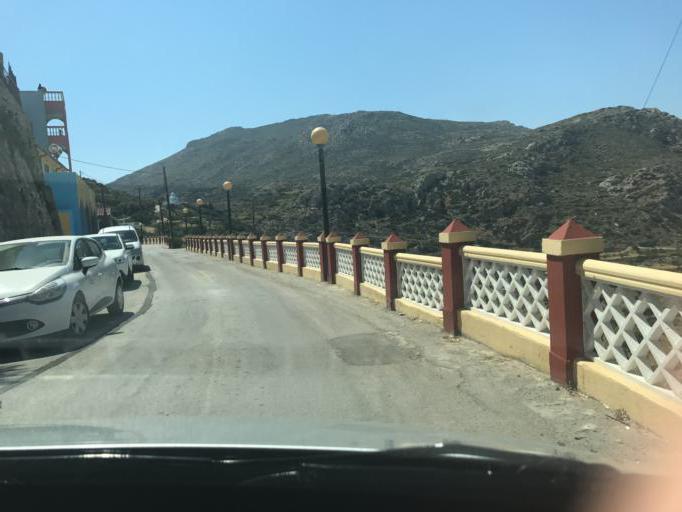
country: GR
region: South Aegean
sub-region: Nomos Dodekanisou
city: Karpathos
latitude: 35.4911
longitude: 27.1674
